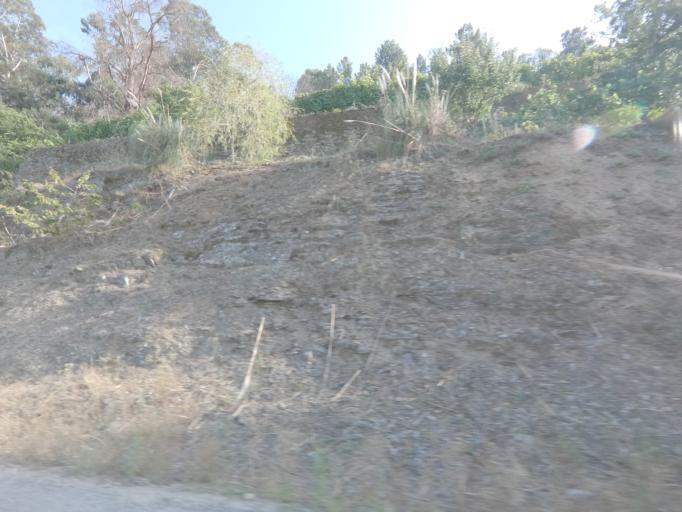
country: PT
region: Viseu
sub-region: Tabuaco
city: Tabuaco
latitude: 41.1297
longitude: -7.5348
